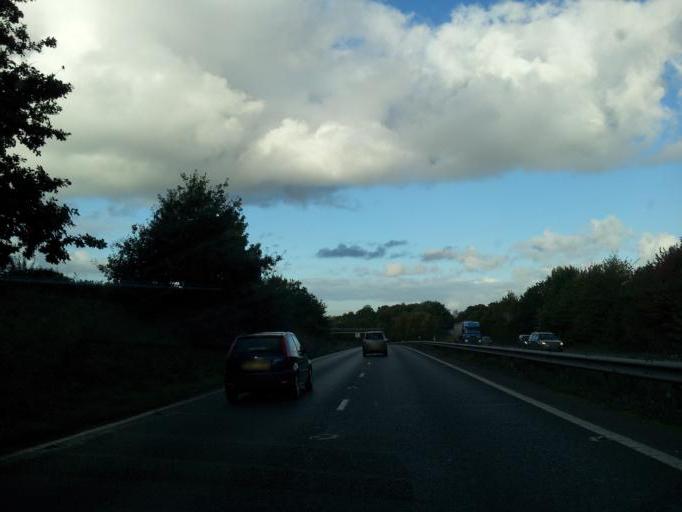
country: GB
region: England
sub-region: Norfolk
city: Brundall
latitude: 52.6379
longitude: 1.4541
